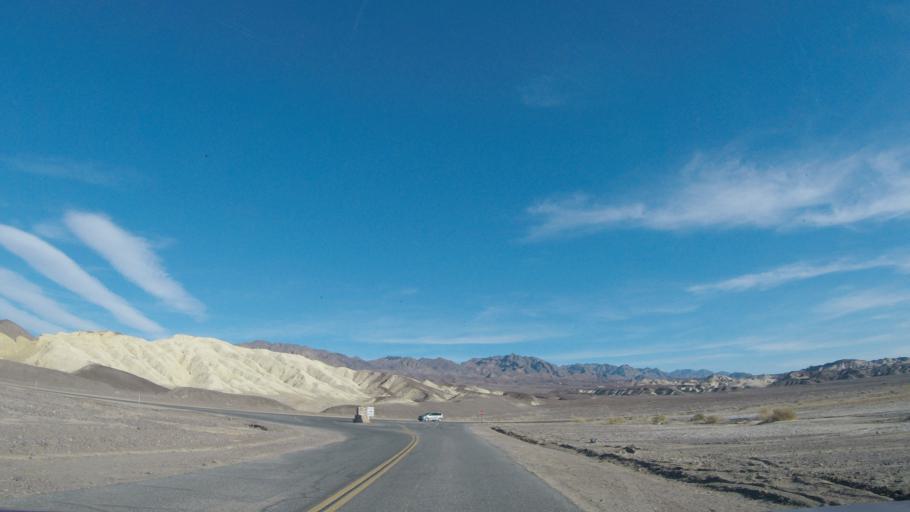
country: US
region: Nevada
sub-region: Nye County
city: Beatty
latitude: 36.4799
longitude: -116.8708
